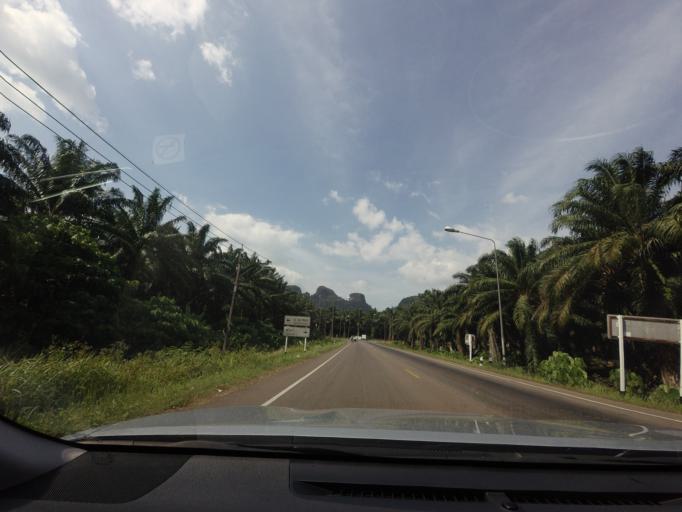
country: TH
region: Phangnga
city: Ban Ao Nang
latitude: 8.1457
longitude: 98.8117
